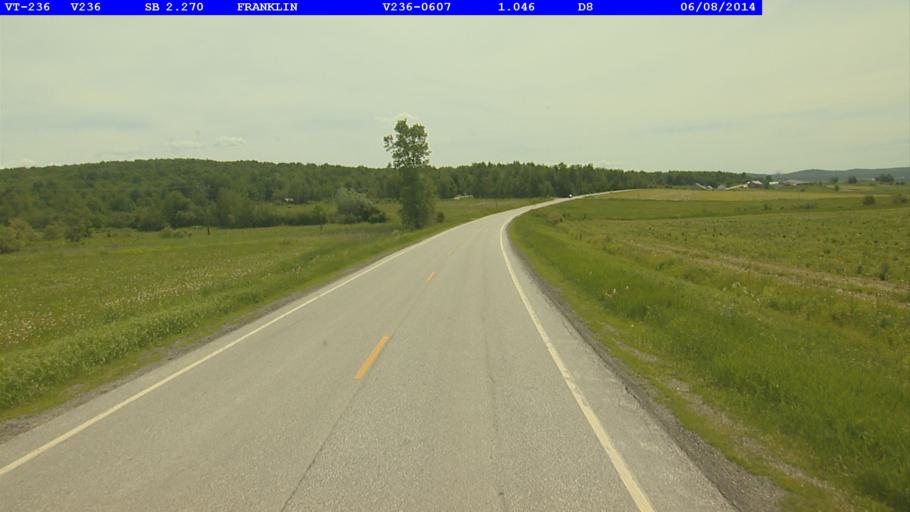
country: US
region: Vermont
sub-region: Franklin County
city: Enosburg Falls
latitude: 44.9432
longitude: -72.8628
